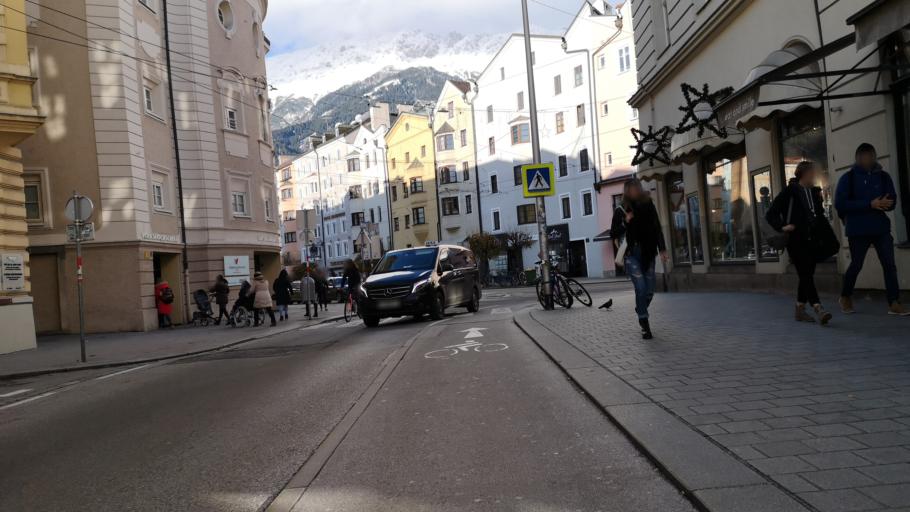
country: AT
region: Tyrol
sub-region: Innsbruck Stadt
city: Innsbruck
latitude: 47.2663
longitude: 11.3923
